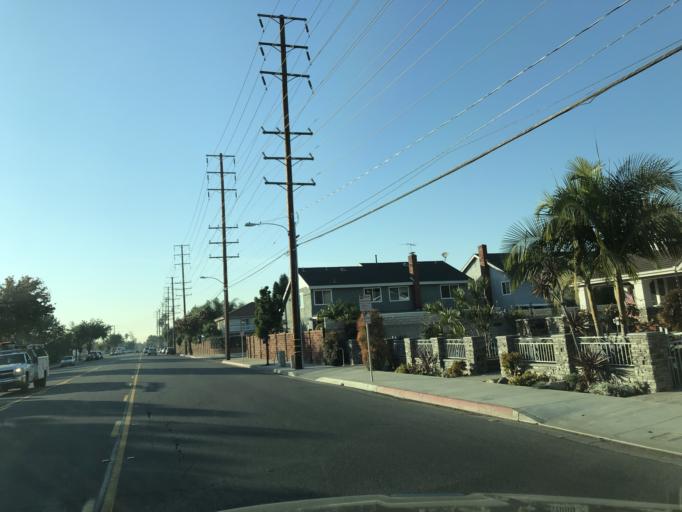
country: US
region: California
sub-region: Orange County
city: Orange
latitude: 33.7672
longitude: -117.8473
